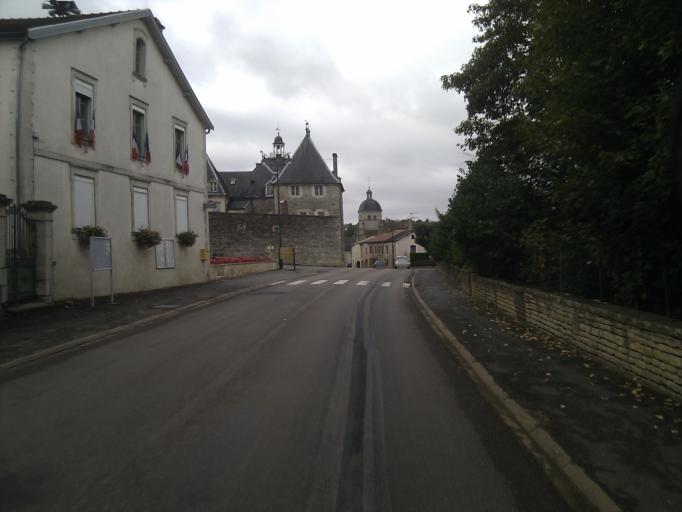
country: FR
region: Champagne-Ardenne
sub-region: Departement de la Haute-Marne
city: Doulaincourt-Saucourt
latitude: 48.2516
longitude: 5.3305
